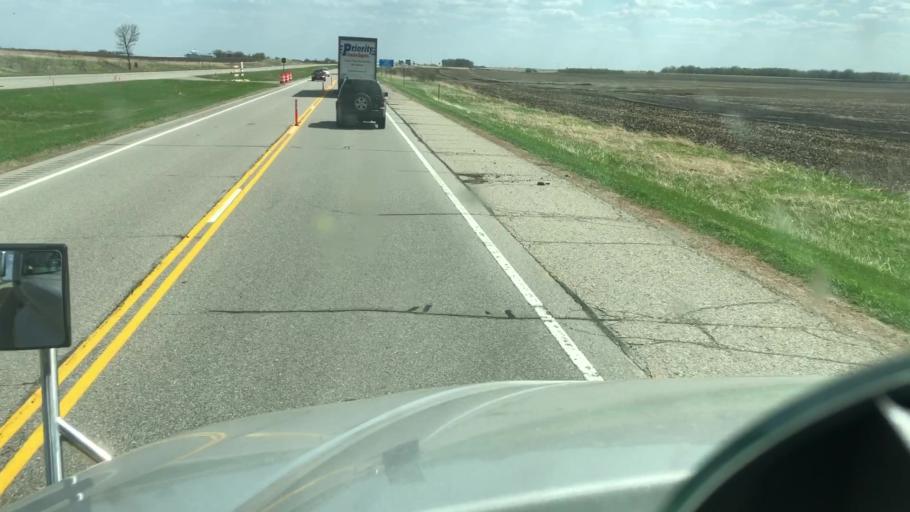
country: US
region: Minnesota
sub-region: Scott County
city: Belle Plaine
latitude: 44.5556
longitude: -93.8508
